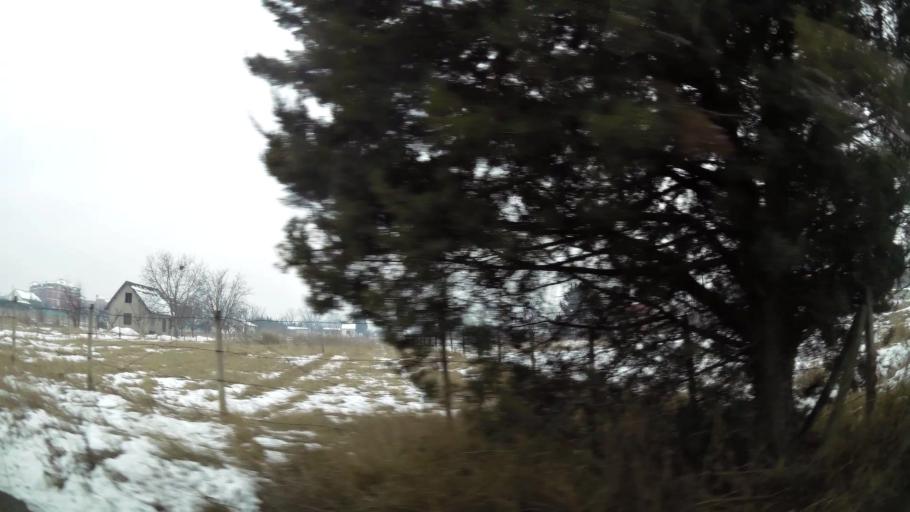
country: MK
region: Cucer-Sandevo
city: Chucher - Sandevo
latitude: 42.0525
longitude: 21.3645
